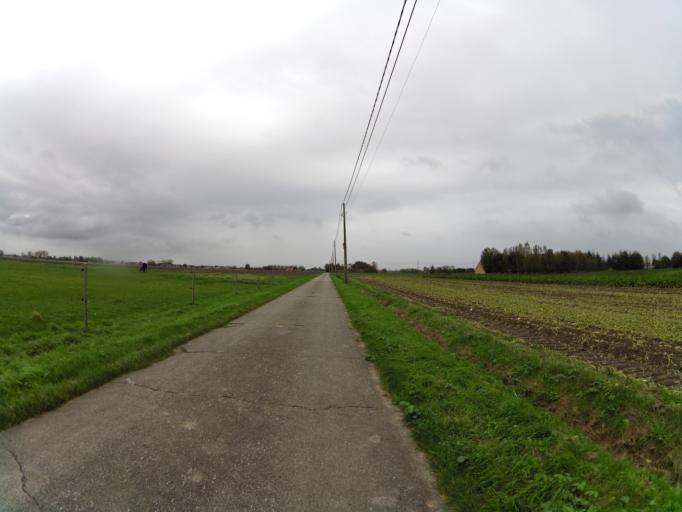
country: BE
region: Flanders
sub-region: Provincie West-Vlaanderen
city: Gistel
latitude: 51.1238
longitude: 2.9293
